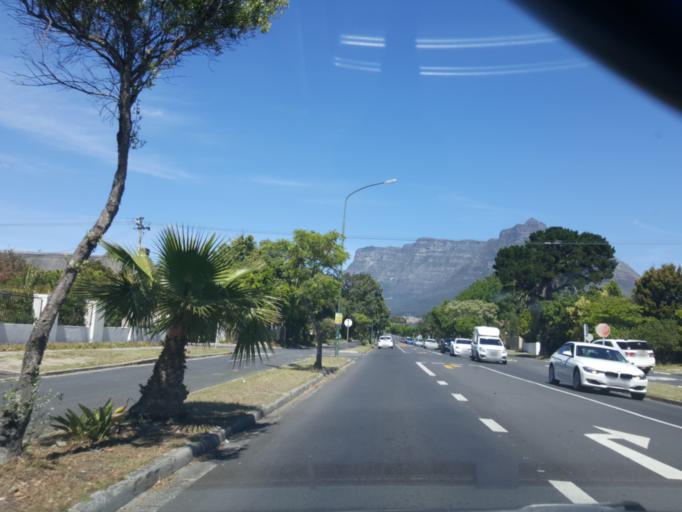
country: ZA
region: Western Cape
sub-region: City of Cape Town
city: Rosebank
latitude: -33.9431
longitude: 18.4958
